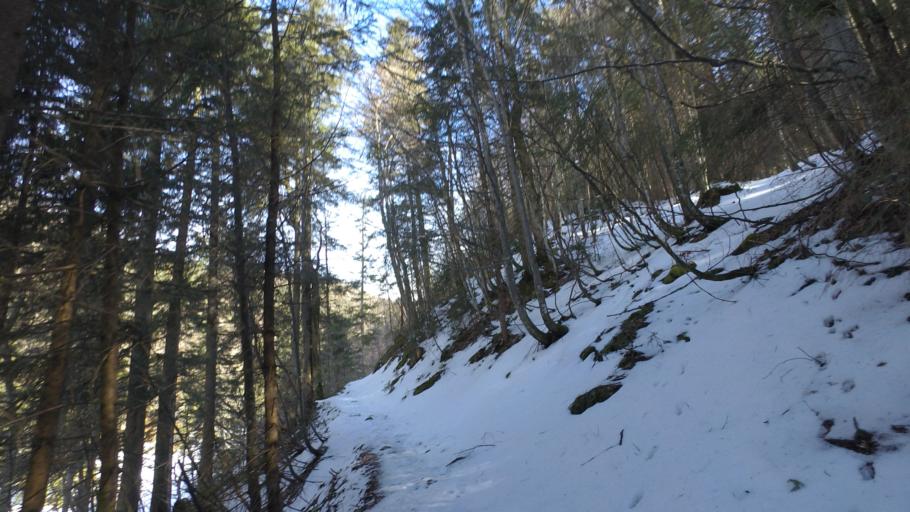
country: DE
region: Bavaria
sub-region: Upper Bavaria
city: Reit im Winkl
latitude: 47.6892
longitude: 12.4451
